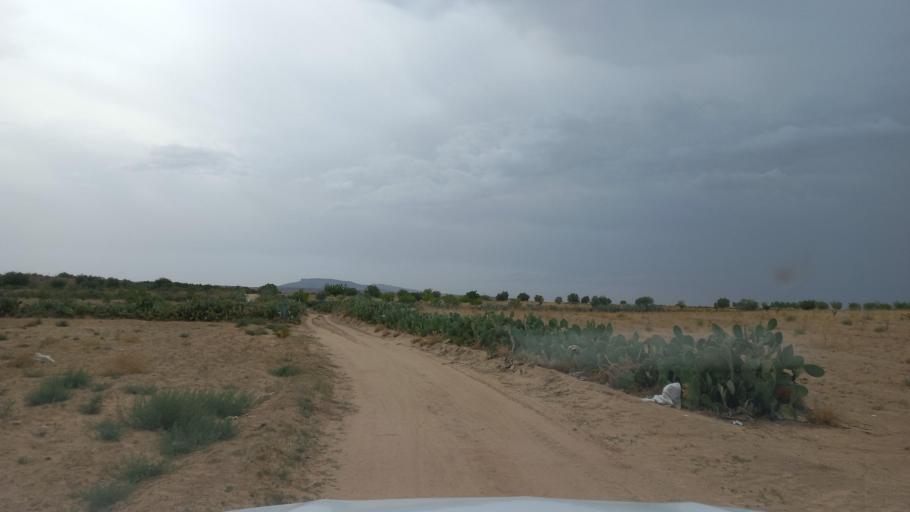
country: TN
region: Al Qasrayn
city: Kasserine
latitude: 35.2392
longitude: 9.0181
